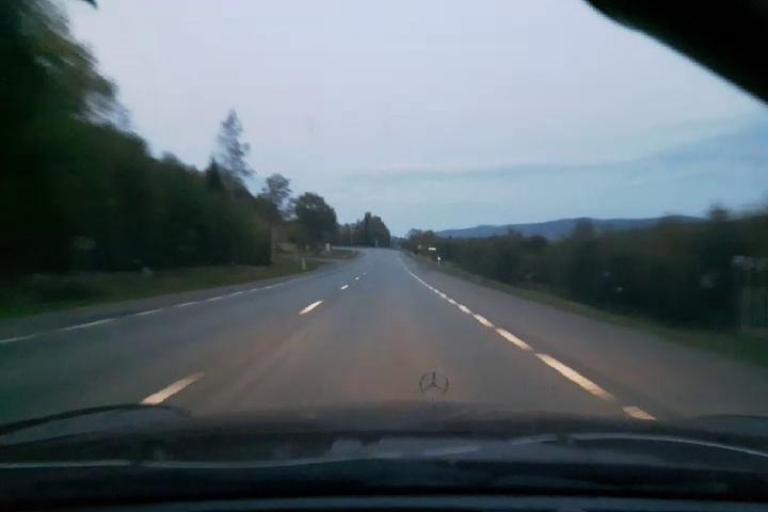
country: SE
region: Vaesternorrland
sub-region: Kramfors Kommun
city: Nordingra
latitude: 63.0050
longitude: 18.2596
